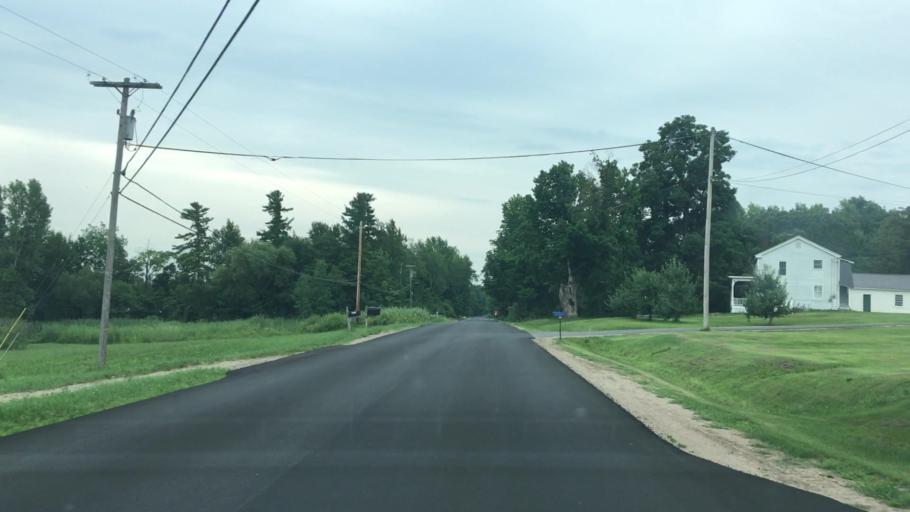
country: US
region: New York
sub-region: Clinton County
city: Peru
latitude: 44.5662
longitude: -73.5695
